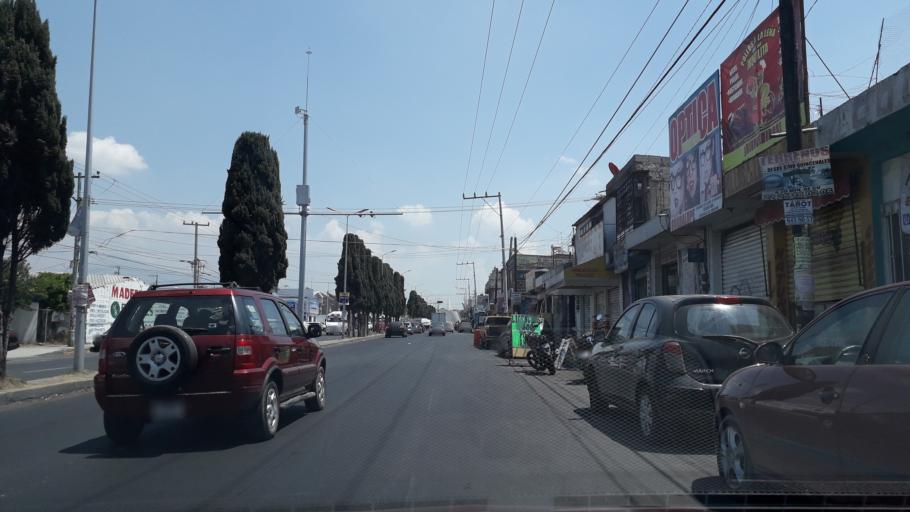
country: MX
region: Puebla
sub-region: Amozoc
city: Casa Blanca
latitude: 19.0645
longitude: -98.1225
